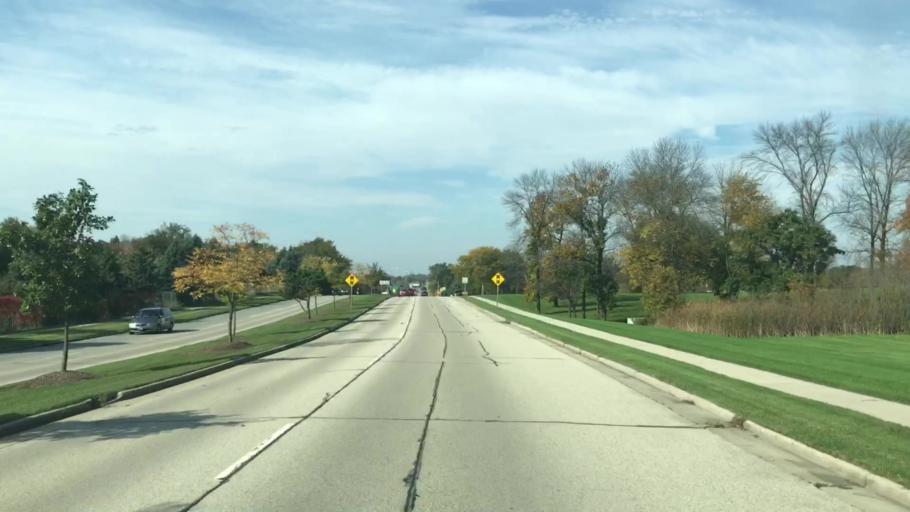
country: US
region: Wisconsin
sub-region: Ozaukee County
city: Thiensville
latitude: 43.2217
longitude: -87.9701
